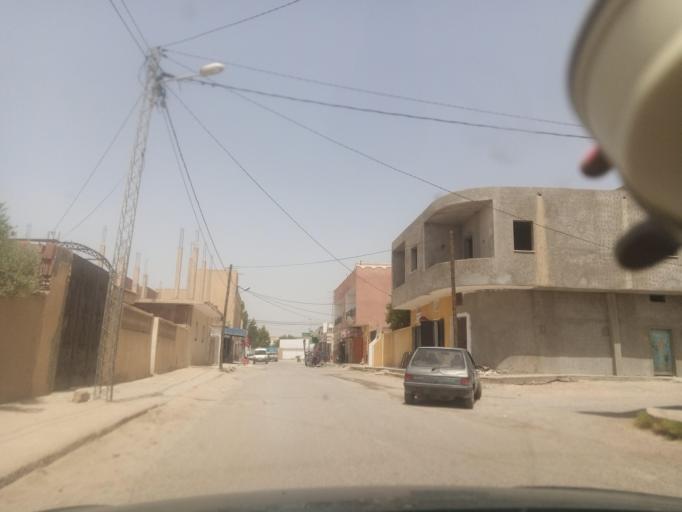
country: TN
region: Al Qasrayn
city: Kasserine
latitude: 35.2126
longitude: 8.8971
